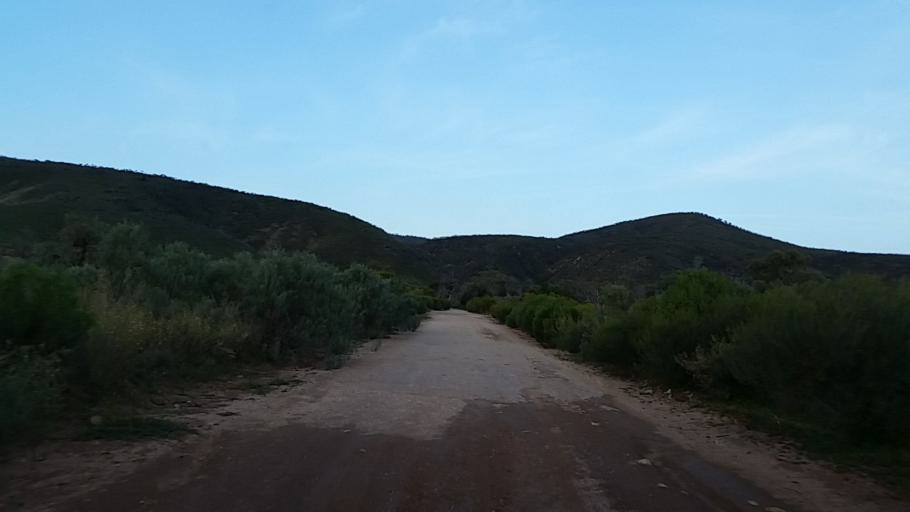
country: AU
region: South Australia
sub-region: Port Pirie City and Dists
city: Port Pirie
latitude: -33.0253
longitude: 138.0934
